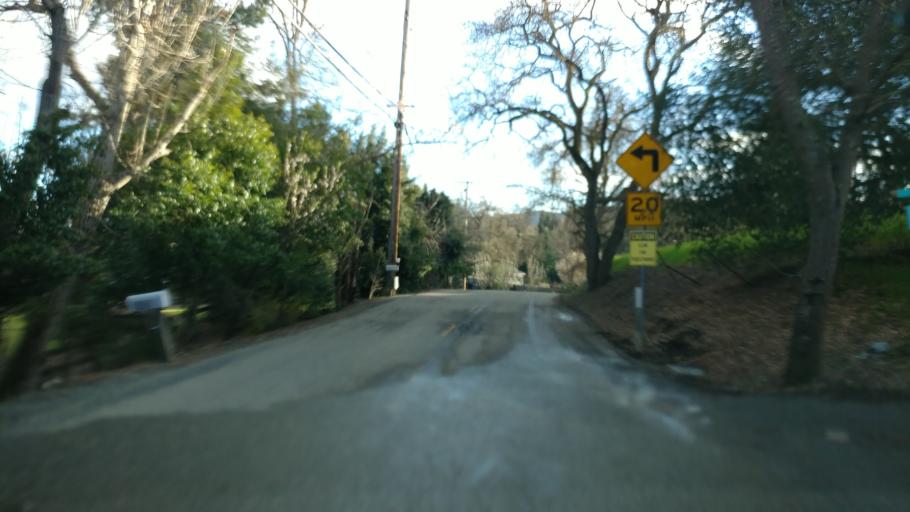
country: US
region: California
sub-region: Contra Costa County
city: Danville
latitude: 37.8395
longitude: -122.0005
